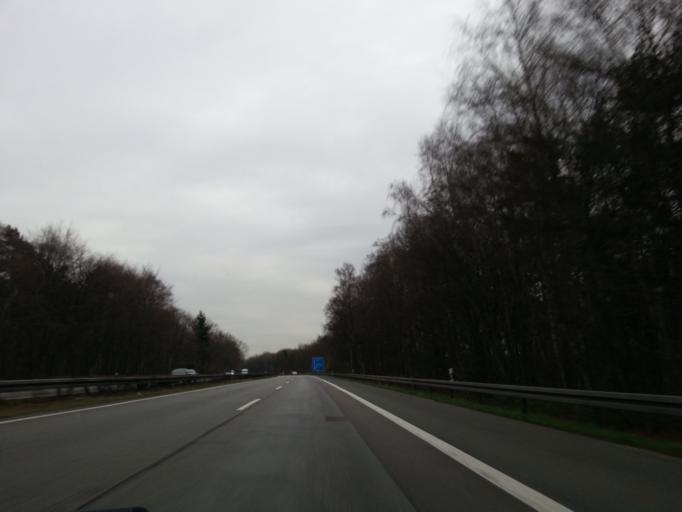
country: DE
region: North Rhine-Westphalia
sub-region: Regierungsbezirk Dusseldorf
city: Dinslaken
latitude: 51.5945
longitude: 6.7824
